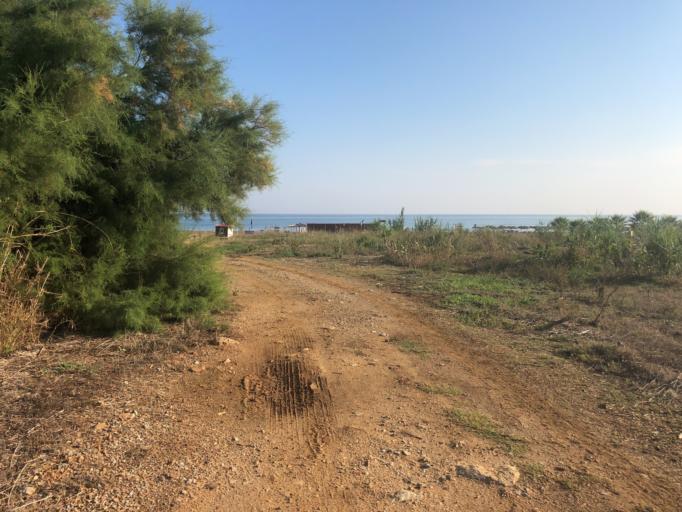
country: GR
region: Crete
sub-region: Nomos Chanias
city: Georgioupolis
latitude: 35.3538
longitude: 24.2861
